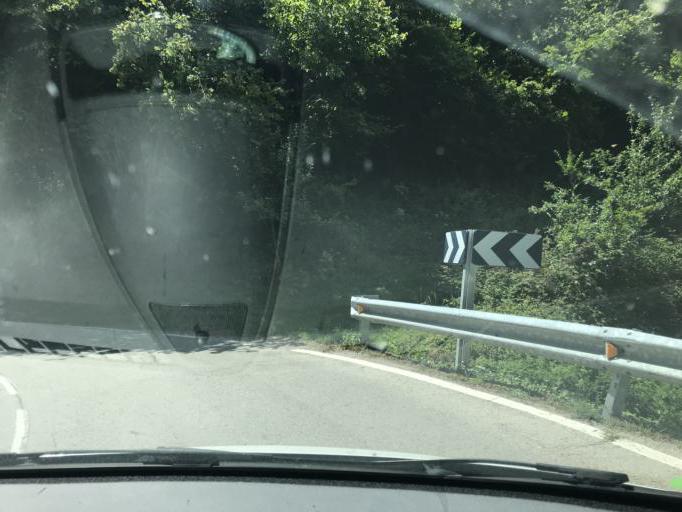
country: ES
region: Cantabria
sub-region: Provincia de Cantabria
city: Cabezon de Liebana
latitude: 43.0773
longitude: -4.4985
